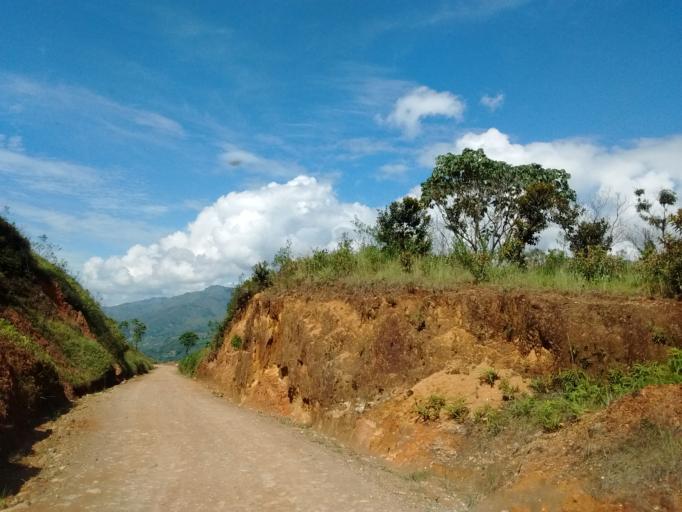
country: CO
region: Cauca
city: Morales
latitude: 2.6876
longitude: -76.7471
